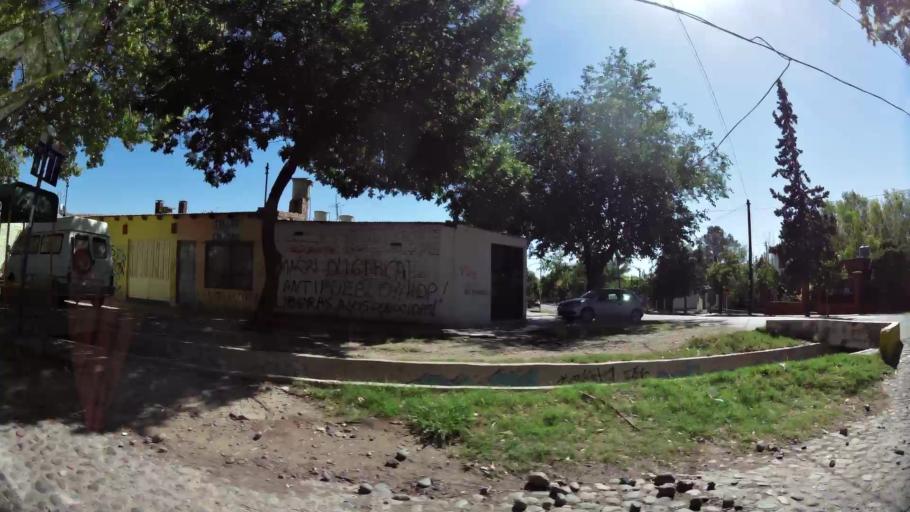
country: AR
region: Mendoza
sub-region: Departamento de Godoy Cruz
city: Godoy Cruz
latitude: -32.9454
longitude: -68.8089
